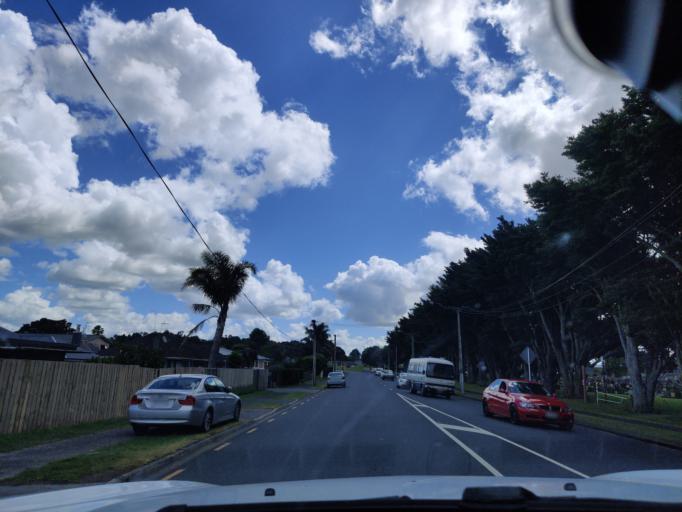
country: NZ
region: Auckland
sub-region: Auckland
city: Papakura
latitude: -37.0701
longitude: 174.9457
